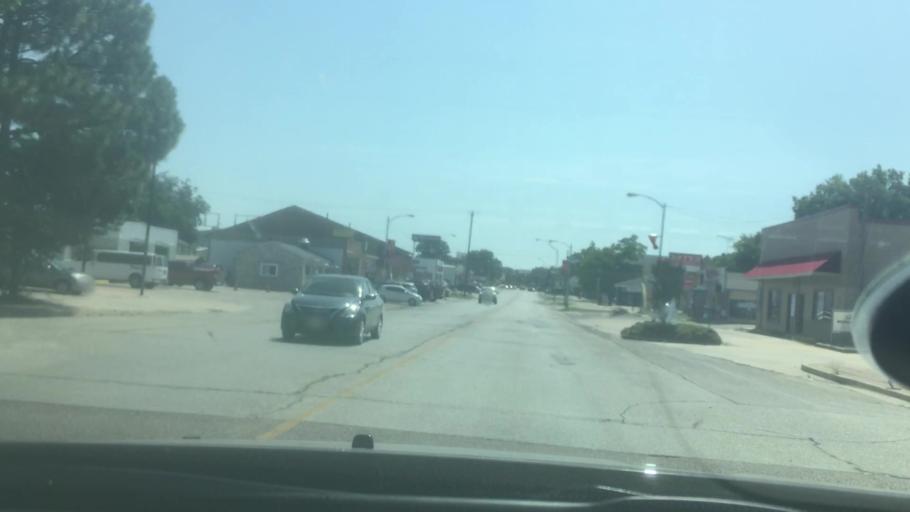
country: US
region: Oklahoma
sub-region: Pontotoc County
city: Ada
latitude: 34.7745
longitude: -96.6738
